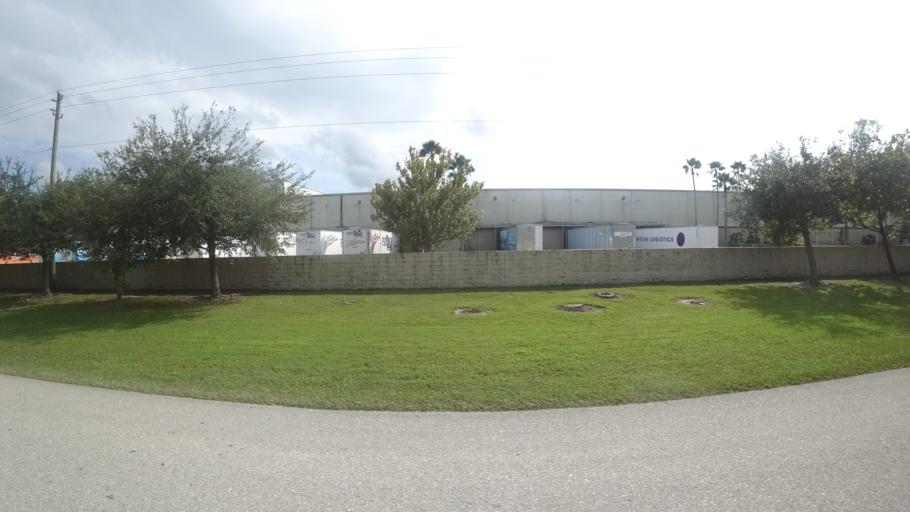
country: US
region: Florida
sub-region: Manatee County
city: Samoset
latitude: 27.4572
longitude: -82.5367
